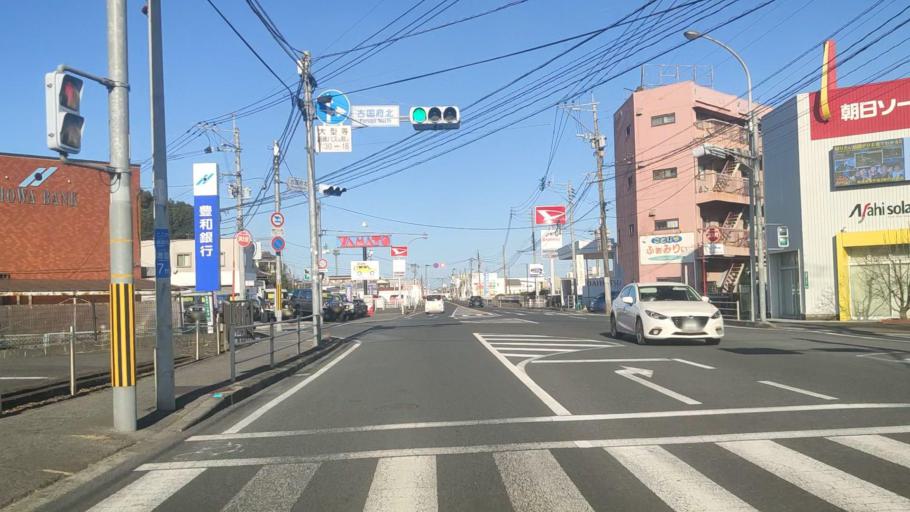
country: JP
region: Oita
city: Oita
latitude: 33.2176
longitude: 131.6138
